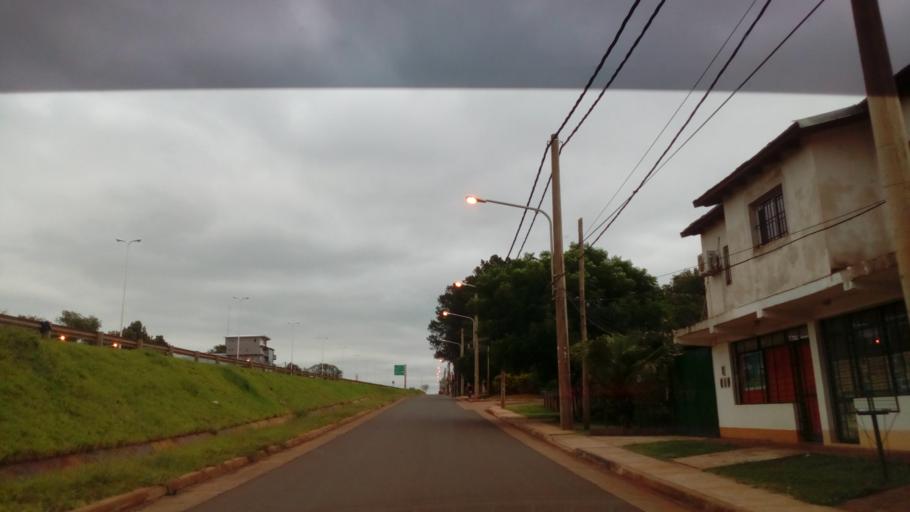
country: AR
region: Misiones
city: Garupa
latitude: -27.4569
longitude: -55.8547
